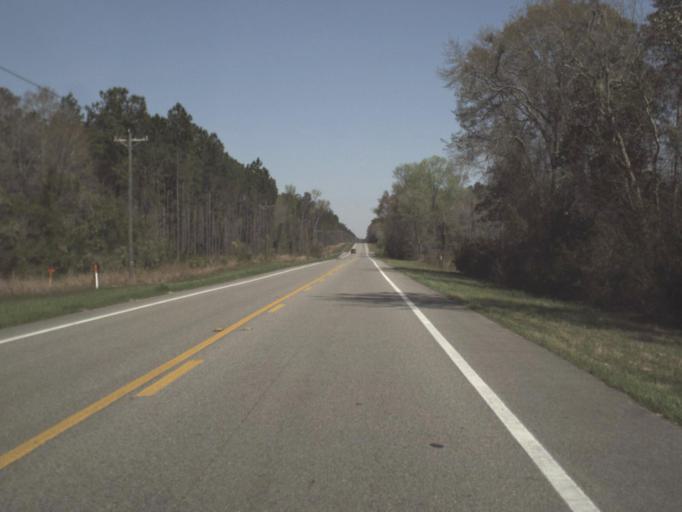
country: US
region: Florida
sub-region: Gadsden County
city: Gretna
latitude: 30.3851
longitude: -84.7185
